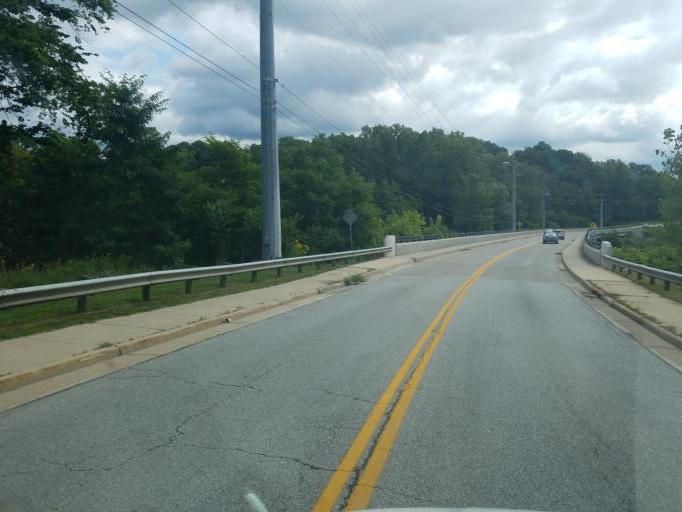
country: US
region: Ohio
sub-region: Lake County
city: Painesville
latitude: 41.7196
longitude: -81.2286
